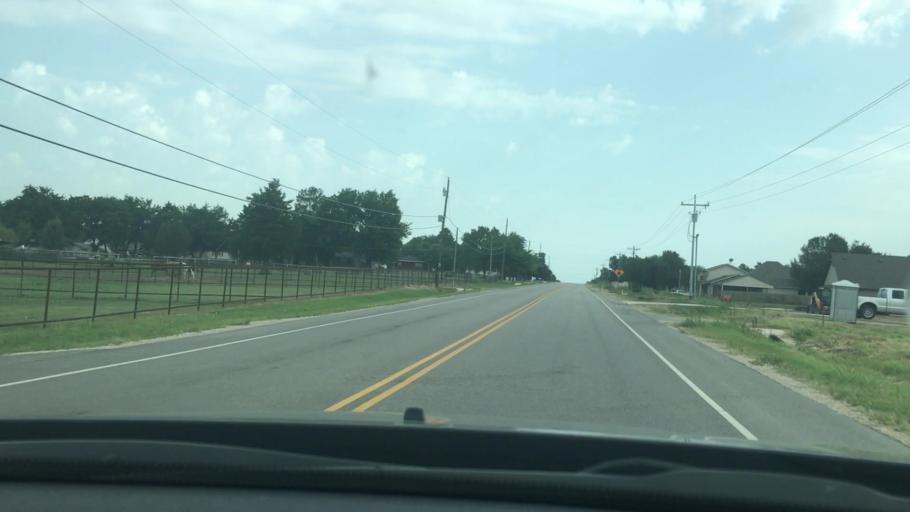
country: US
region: Oklahoma
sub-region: Pontotoc County
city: Ada
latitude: 34.8067
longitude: -96.6523
